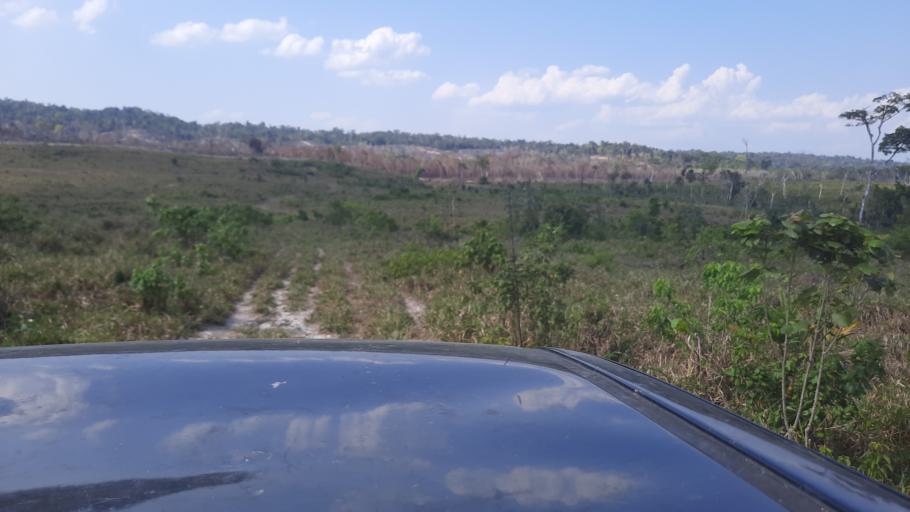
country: BZ
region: Cayo
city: Valley of Peace
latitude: 17.4007
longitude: -89.0401
